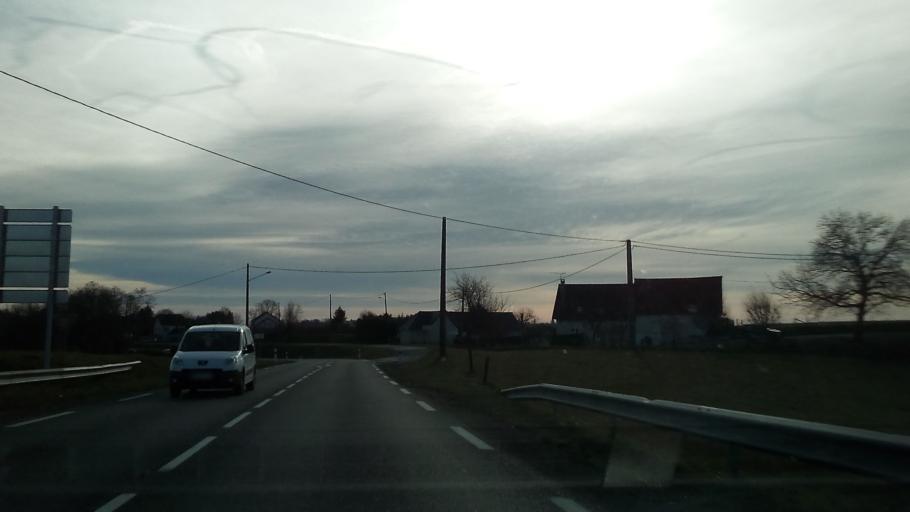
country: FR
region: Limousin
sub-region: Departement de la Correze
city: Seilhac
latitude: 45.3464
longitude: 1.7413
